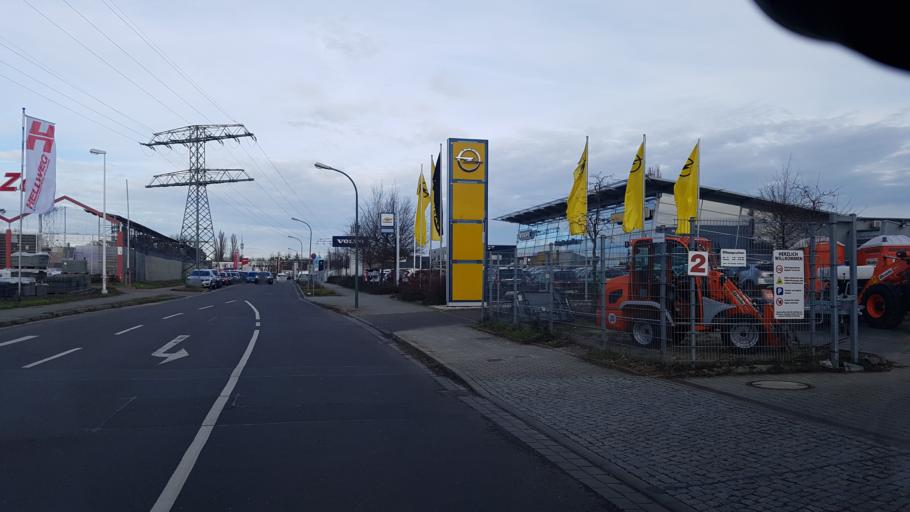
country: DE
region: Brandenburg
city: Potsdam
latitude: 52.3774
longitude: 13.1089
